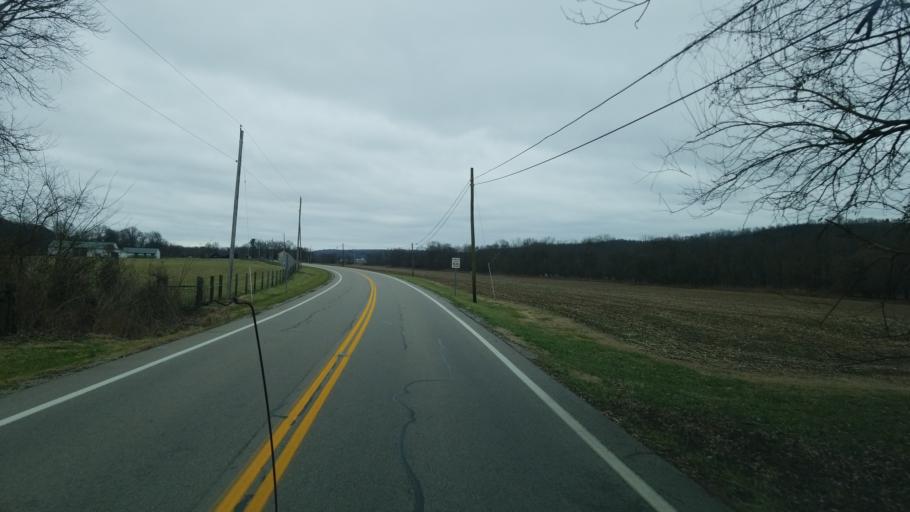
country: US
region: Ohio
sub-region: Clermont County
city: New Richmond
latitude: 38.8069
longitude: -84.2064
